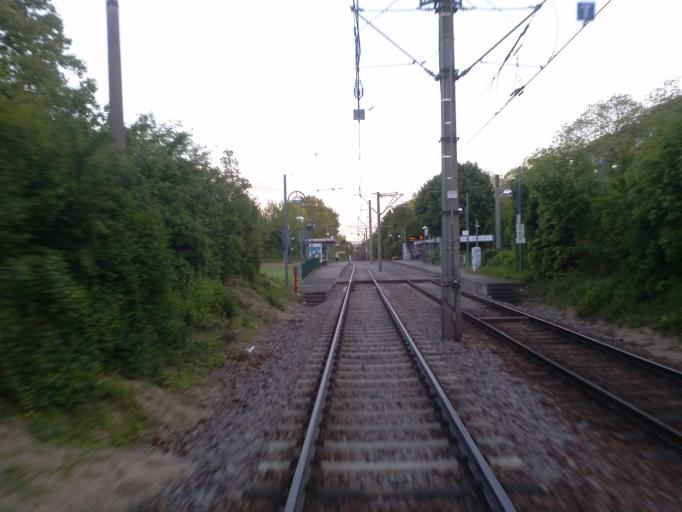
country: DE
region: Baden-Wuerttemberg
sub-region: Karlsruhe Region
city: Karlsruhe
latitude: 49.0346
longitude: 8.3767
